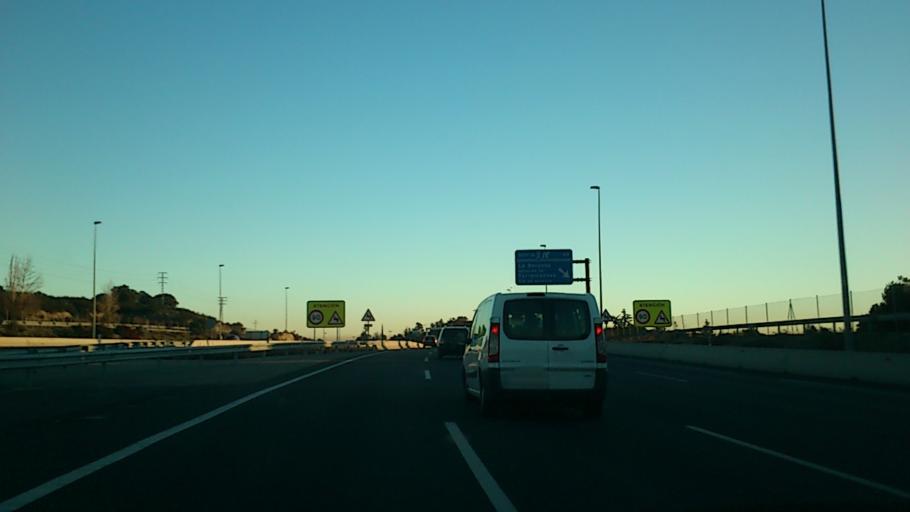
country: ES
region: Madrid
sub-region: Provincia de Madrid
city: Torrelodones
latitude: 40.6016
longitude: -3.9639
